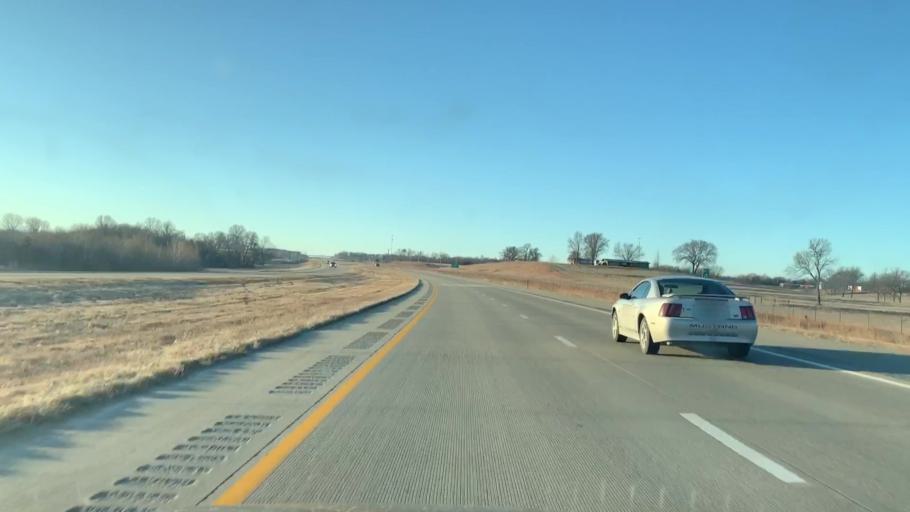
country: US
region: Kansas
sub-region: Linn County
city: Pleasanton
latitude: 38.1365
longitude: -94.7134
